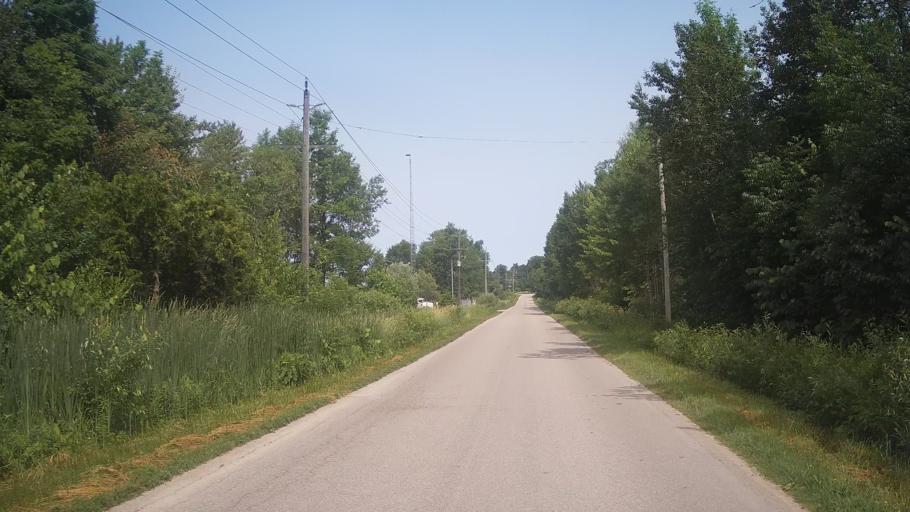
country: CA
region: Ontario
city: Barrie
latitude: 44.4557
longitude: -79.6304
